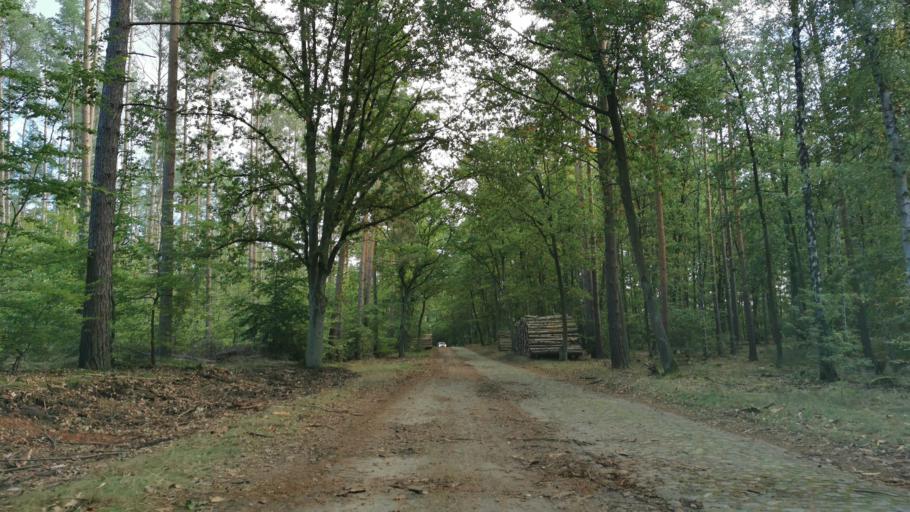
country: DE
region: Brandenburg
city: Michendorf
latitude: 52.3144
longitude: 12.9722
